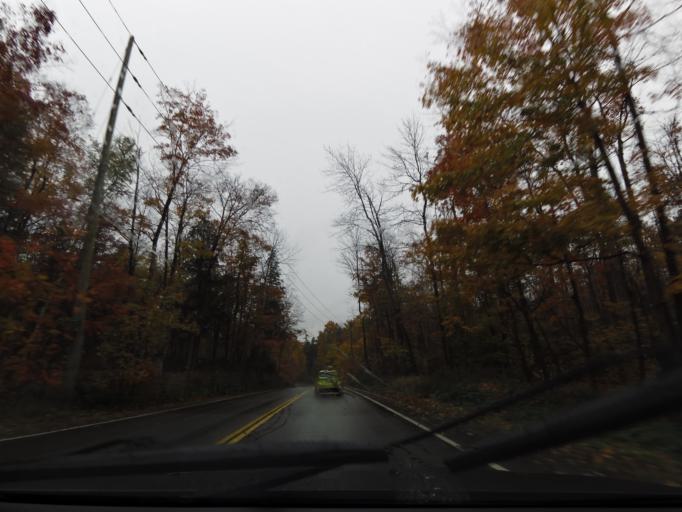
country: CA
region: Ontario
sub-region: Halton
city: Milton
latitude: 43.4616
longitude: -79.9463
